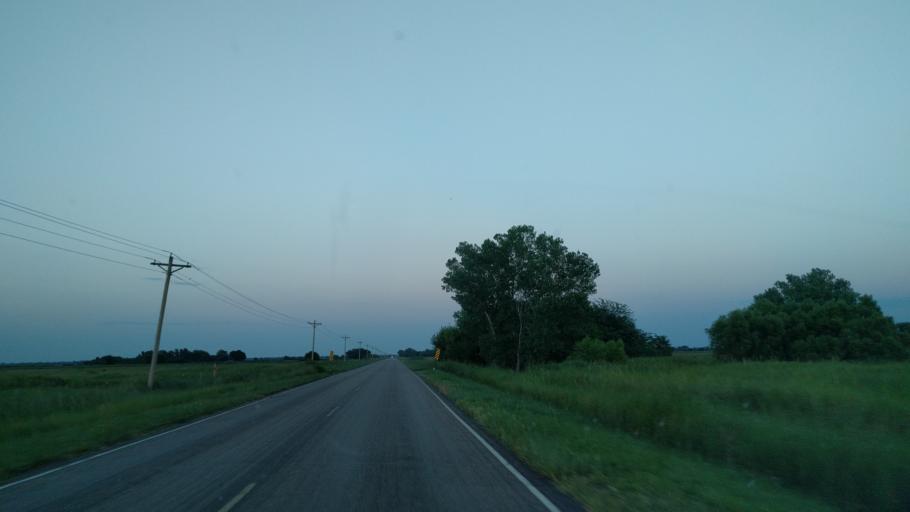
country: US
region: Kansas
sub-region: Reno County
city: Nickerson
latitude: 38.2176
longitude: -98.1217
